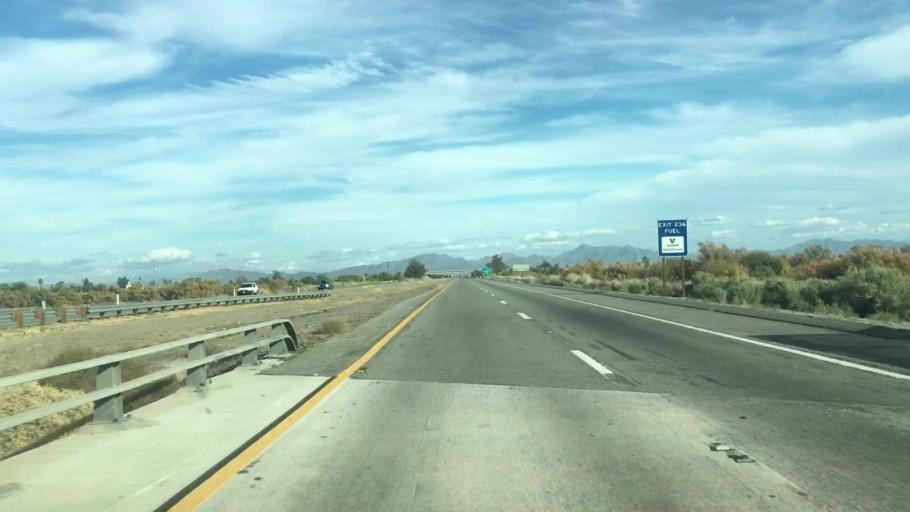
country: US
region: California
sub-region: Riverside County
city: Mesa Verde
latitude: 33.6065
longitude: -114.6680
